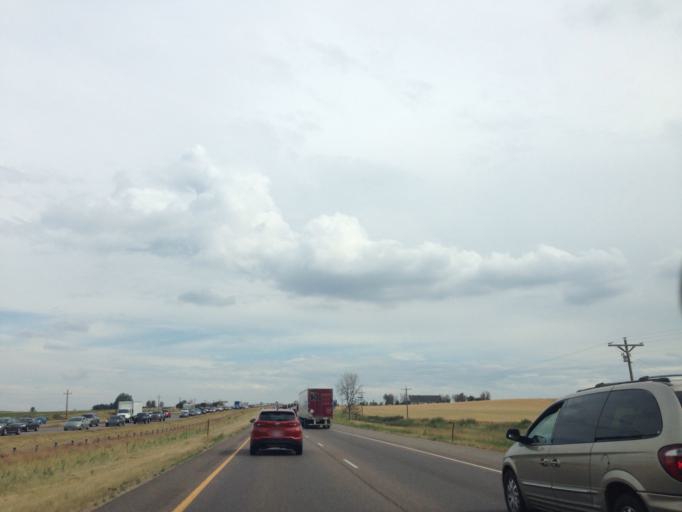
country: US
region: Colorado
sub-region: Weld County
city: Johnstown
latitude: 40.3714
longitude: -104.9899
